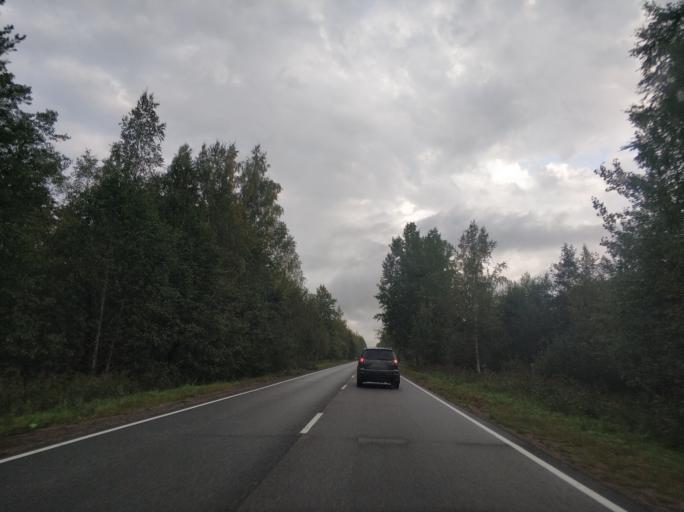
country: RU
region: Leningrad
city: Borisova Griva
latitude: 60.1385
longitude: 30.9547
